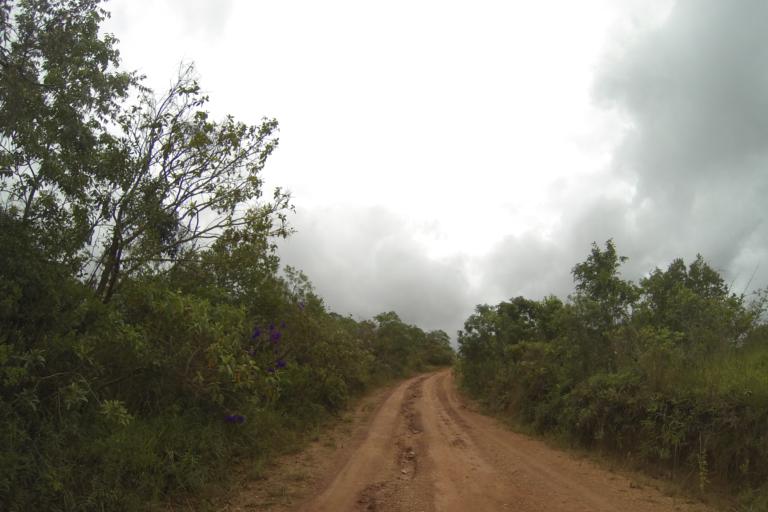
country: BR
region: Minas Gerais
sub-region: Ibia
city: Ibia
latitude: -19.7443
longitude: -46.5697
